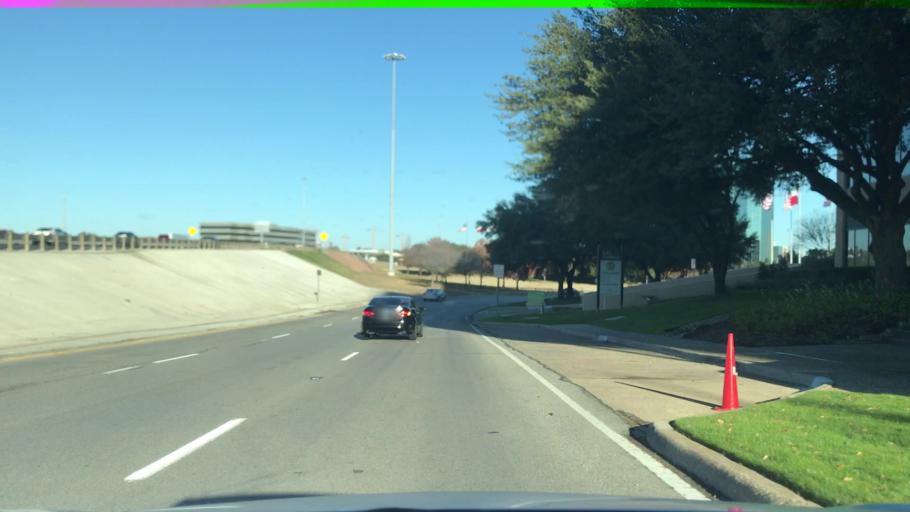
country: US
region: Texas
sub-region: Dallas County
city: Irving
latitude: 32.8663
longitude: -96.9411
